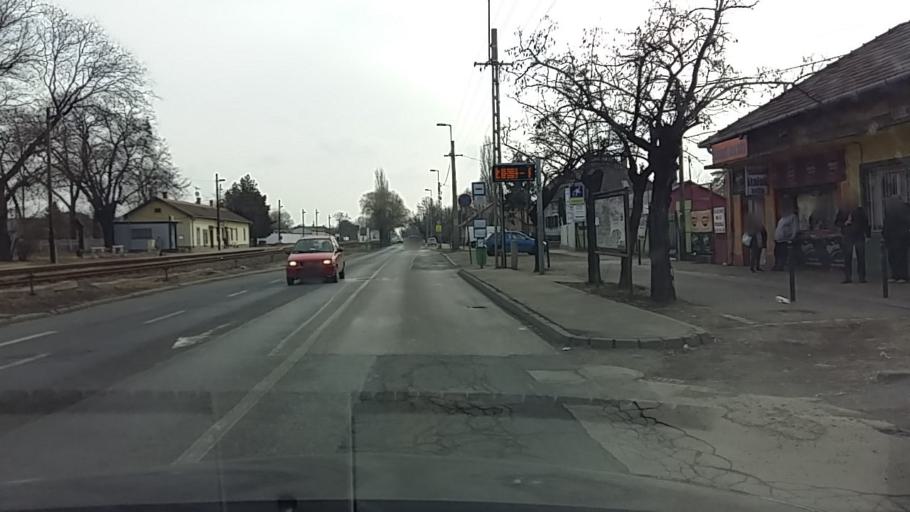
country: HU
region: Pest
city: Gyal
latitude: 47.4036
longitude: 19.1864
